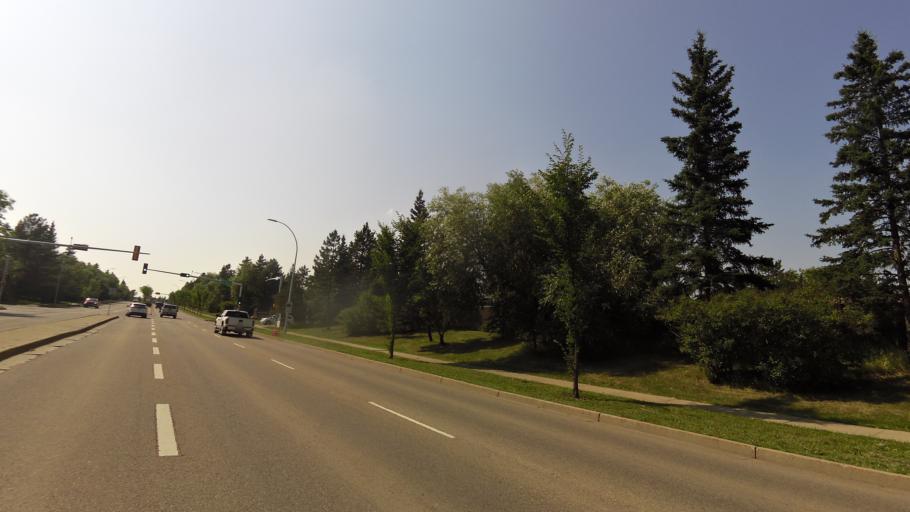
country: CA
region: Alberta
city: St. Albert
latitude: 53.6360
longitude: -113.5826
